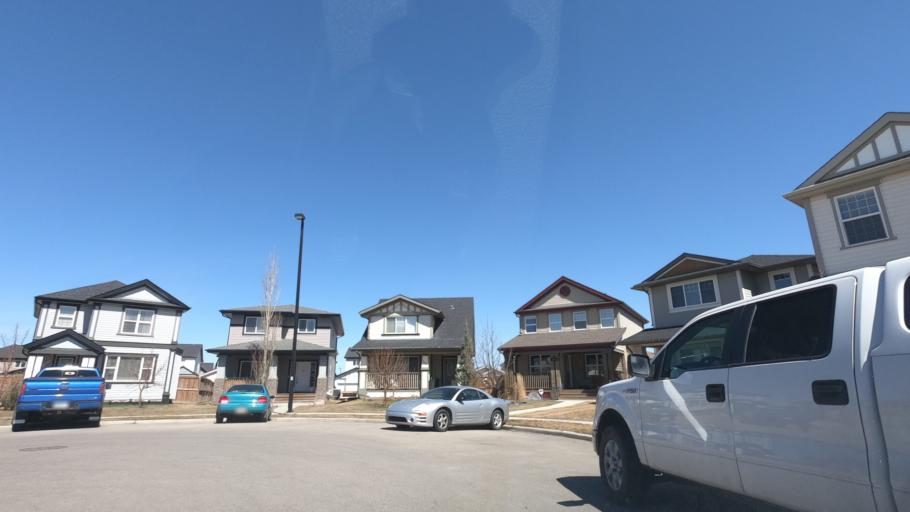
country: CA
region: Alberta
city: Airdrie
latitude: 51.3020
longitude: -114.0423
